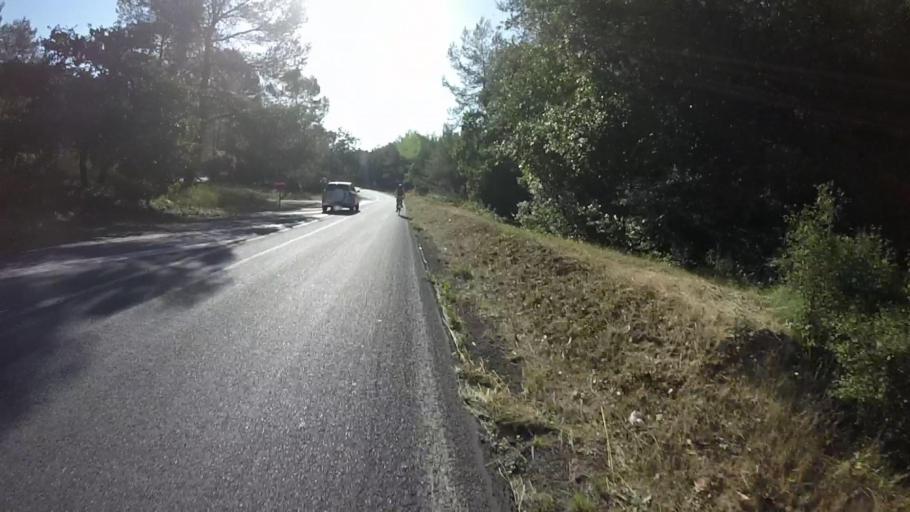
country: FR
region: Provence-Alpes-Cote d'Azur
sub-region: Departement des Alpes-Maritimes
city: Mougins
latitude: 43.6128
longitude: 7.0285
